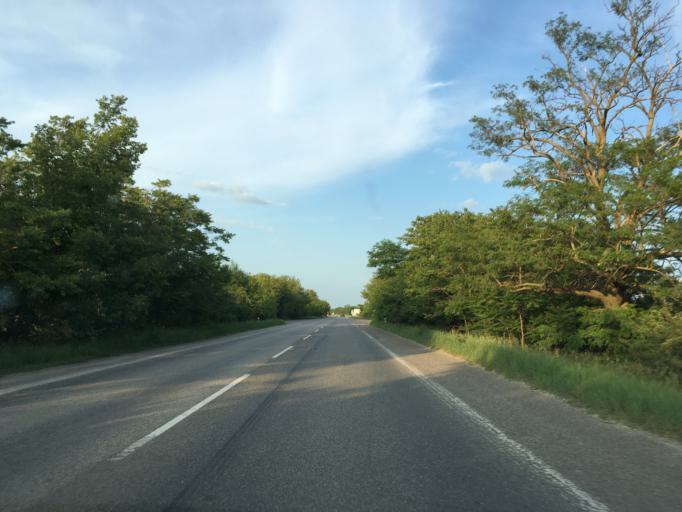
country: SK
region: Bratislavsky
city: Senec
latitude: 48.2058
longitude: 17.4238
